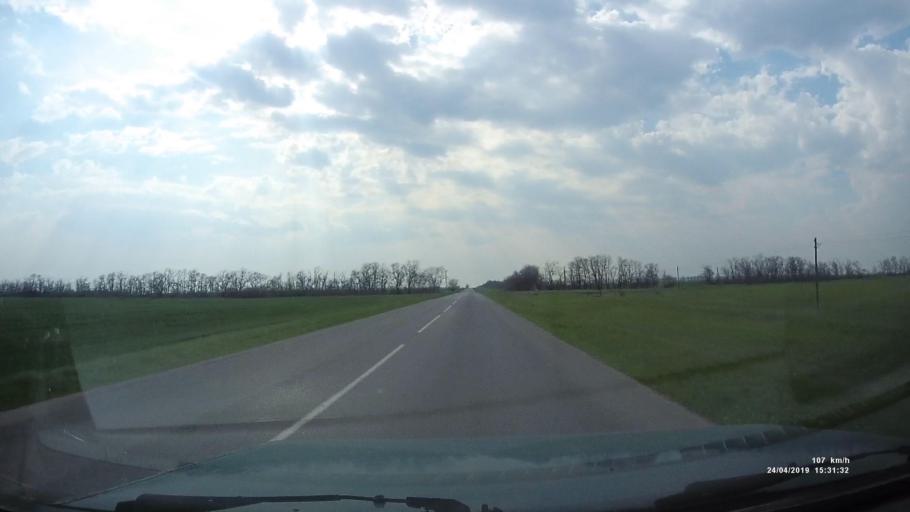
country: RU
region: Rostov
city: Remontnoye
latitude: 46.6001
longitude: 42.9816
